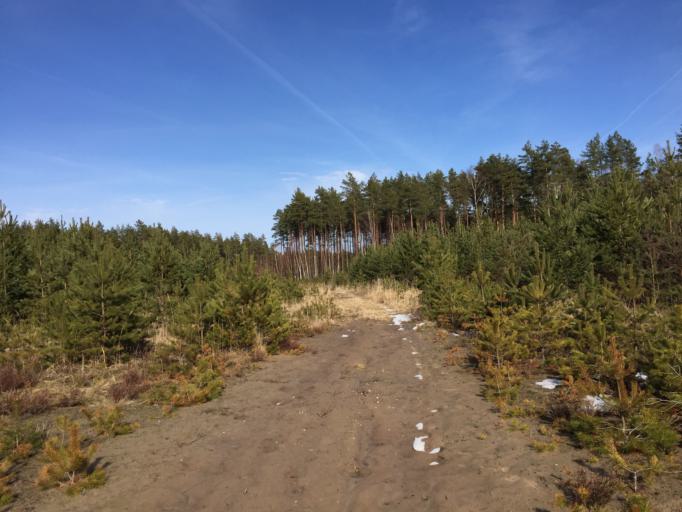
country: EE
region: Paernumaa
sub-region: Paernu linn
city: Parnu
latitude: 58.2337
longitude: 24.5215
